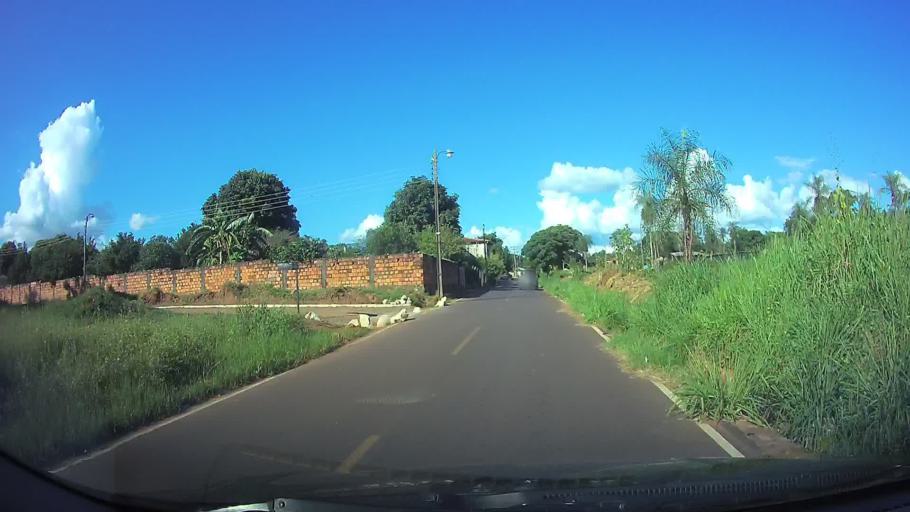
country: PY
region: Central
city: Aregua
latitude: -25.3412
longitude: -57.3863
